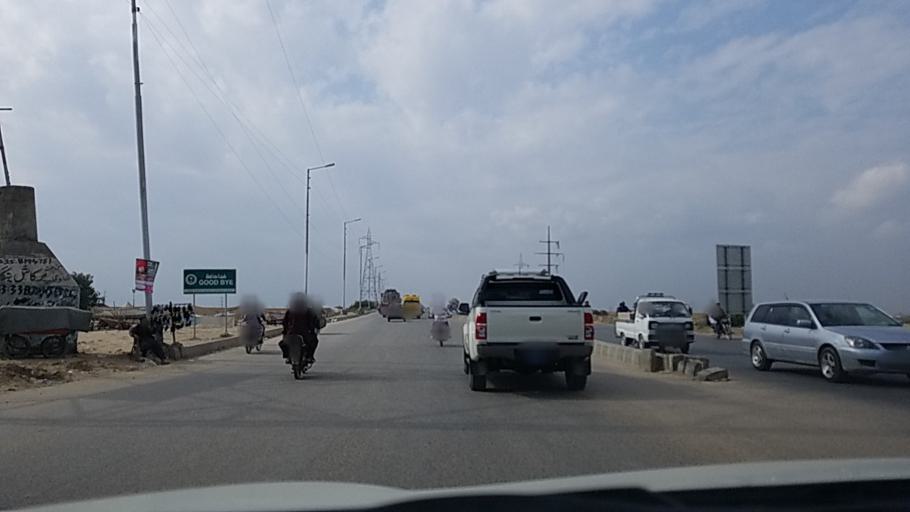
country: PK
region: Sindh
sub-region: Karachi District
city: Karachi
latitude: 24.8204
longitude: 67.1027
